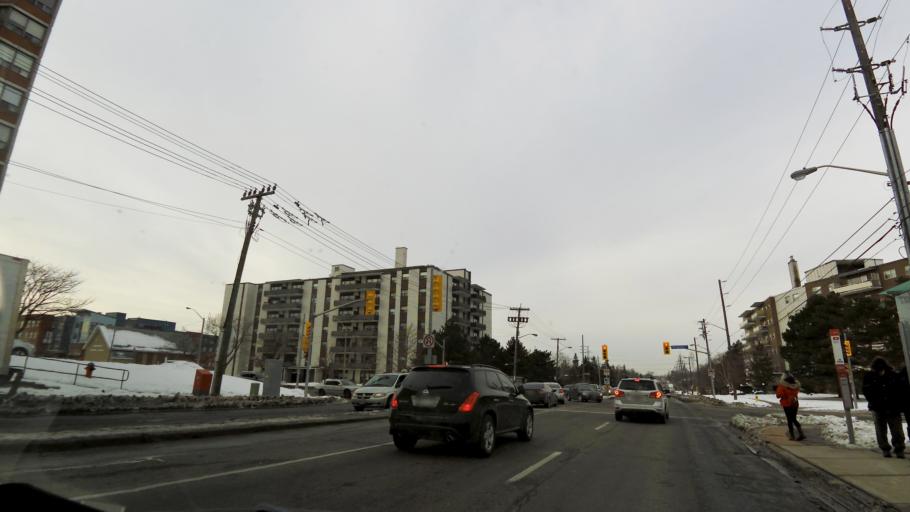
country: CA
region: Ontario
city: Etobicoke
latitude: 43.7167
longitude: -79.5558
